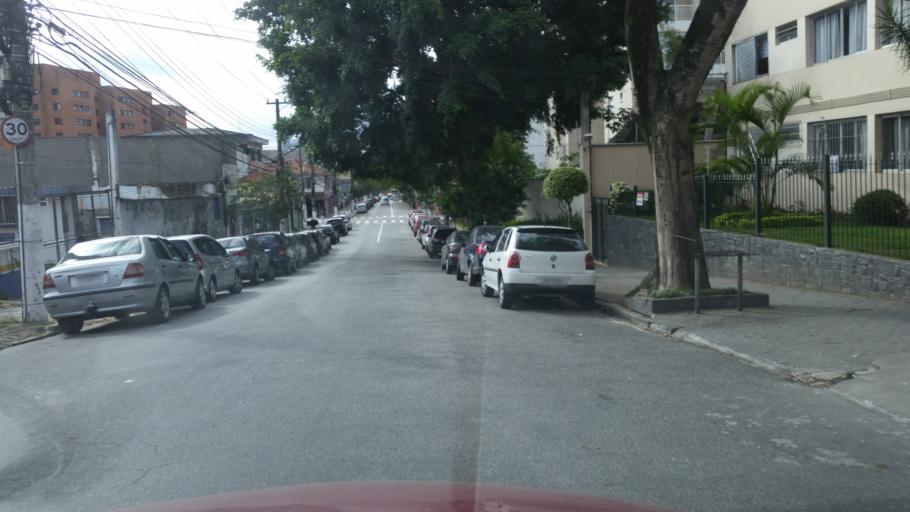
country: BR
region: Sao Paulo
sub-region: Taboao Da Serra
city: Taboao da Serra
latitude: -23.6483
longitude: -46.7047
